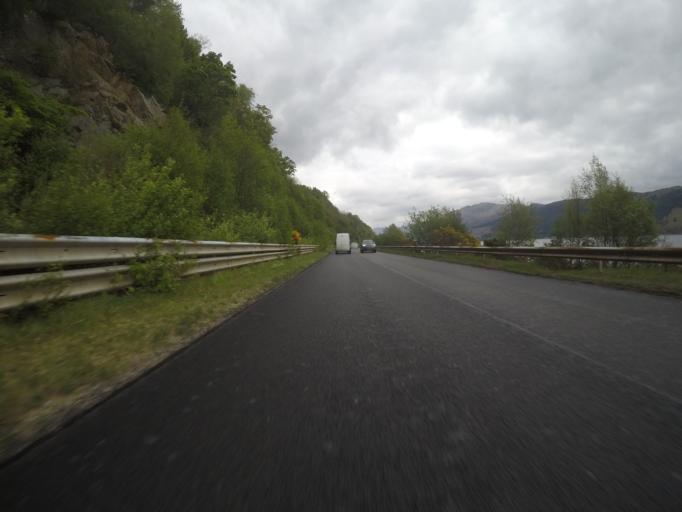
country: GB
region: Scotland
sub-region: Highland
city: Fort William
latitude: 57.2549
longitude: -5.4782
